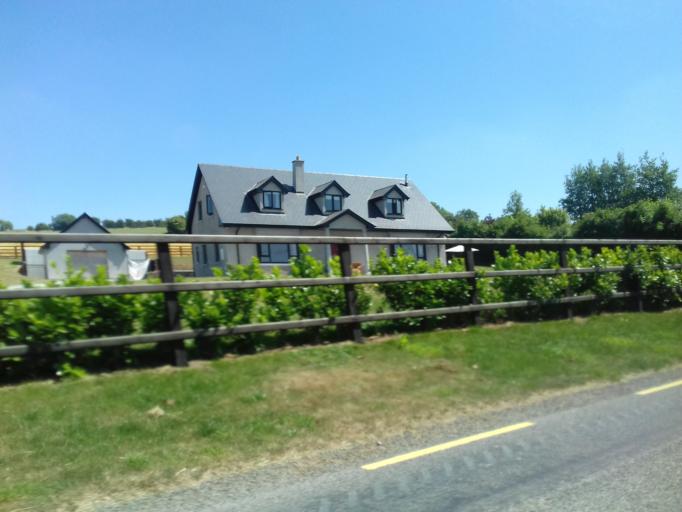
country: IE
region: Leinster
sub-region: An Mhi
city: Stamullin
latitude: 53.5731
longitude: -6.3126
